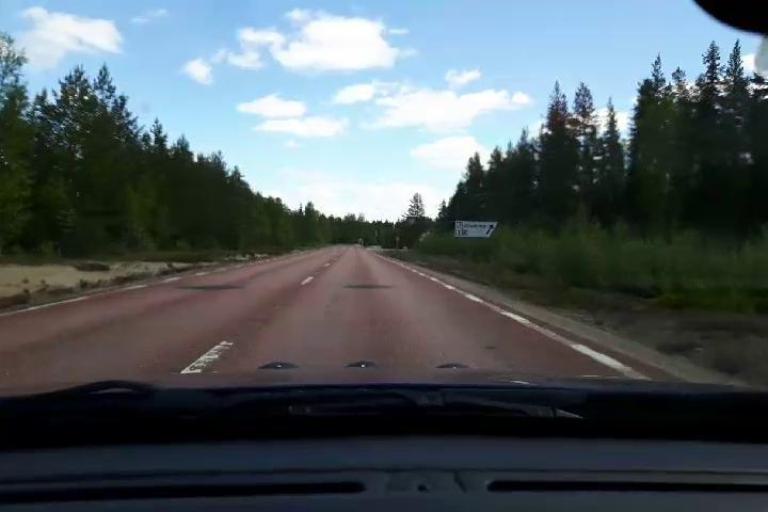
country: SE
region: Gaevleborg
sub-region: Ljusdals Kommun
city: Farila
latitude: 61.9297
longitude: 15.5496
